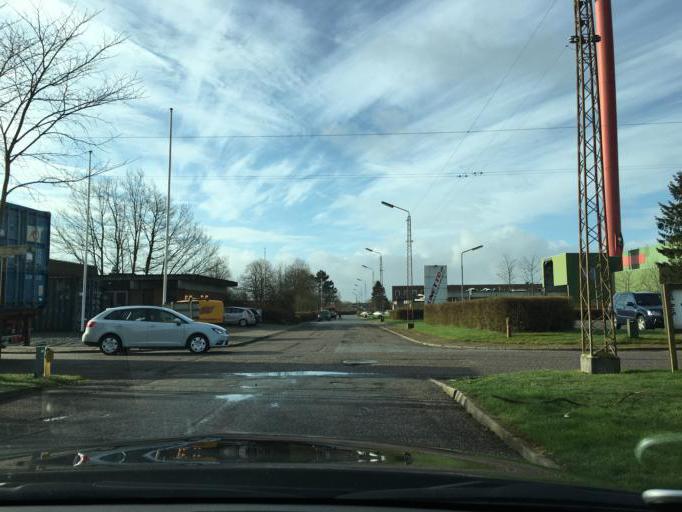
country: DK
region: South Denmark
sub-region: Kolding Kommune
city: Kolding
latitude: 55.5052
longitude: 9.4665
